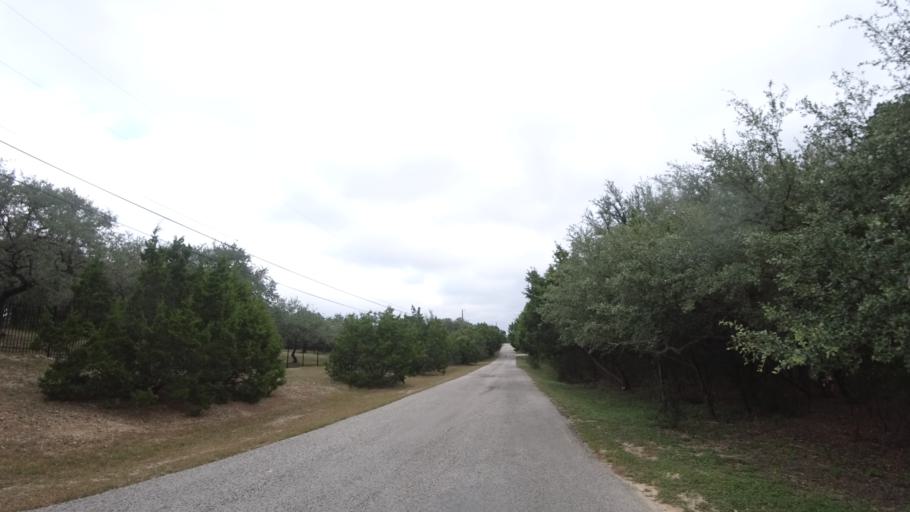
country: US
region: Texas
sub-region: Travis County
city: Bee Cave
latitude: 30.2621
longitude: -97.9201
